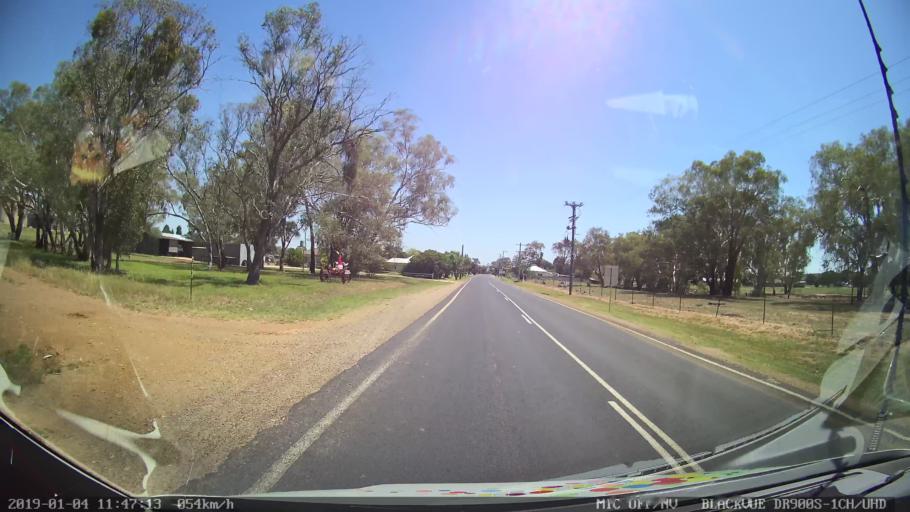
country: AU
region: New South Wales
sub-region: Cabonne
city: Molong
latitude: -32.9345
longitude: 148.7553
